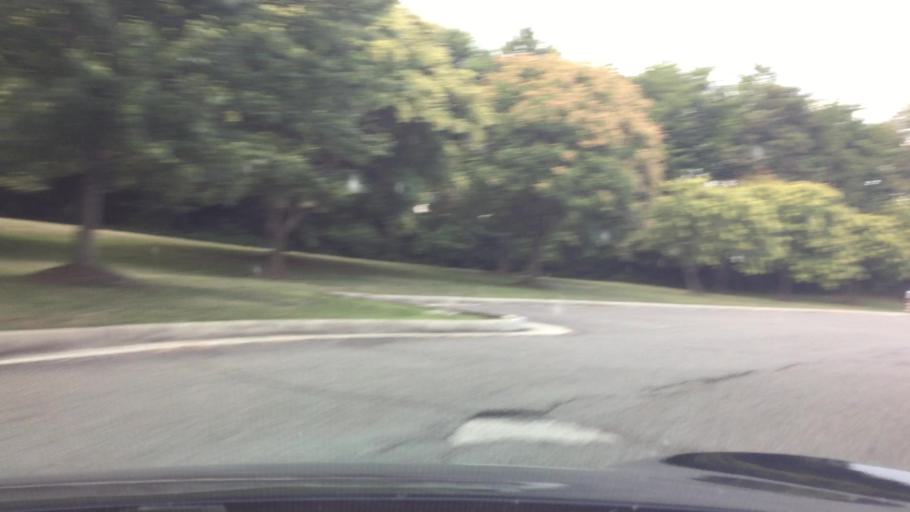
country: US
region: Virginia
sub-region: Pulaski County
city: Dublin
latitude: 37.0938
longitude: -80.6869
